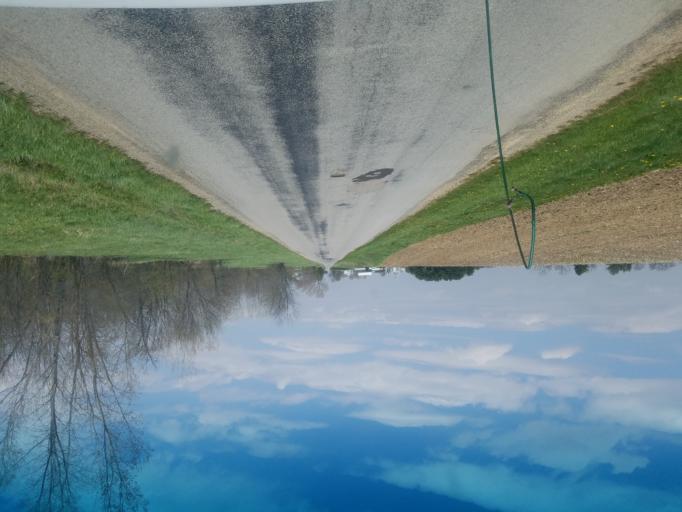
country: US
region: Ohio
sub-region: Wyandot County
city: Upper Sandusky
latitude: 40.7798
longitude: -83.3237
